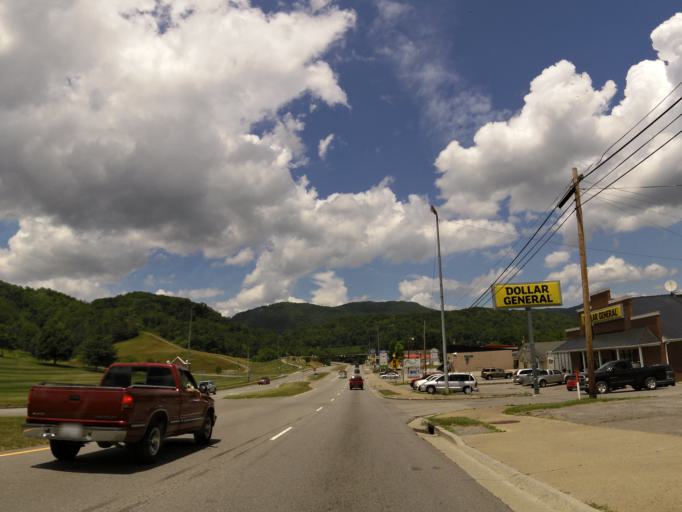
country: US
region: Tennessee
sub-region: Claiborne County
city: Harrogate
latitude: 36.5812
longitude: -83.6564
